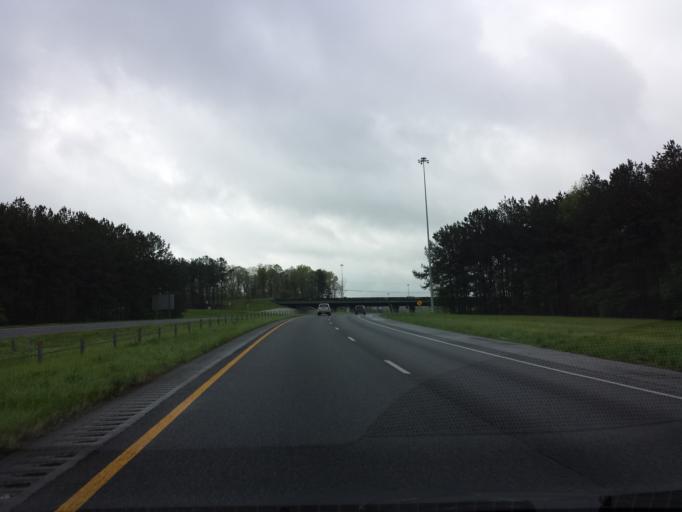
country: US
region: Georgia
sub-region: Cherokee County
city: Canton
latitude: 34.2411
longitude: -84.4663
